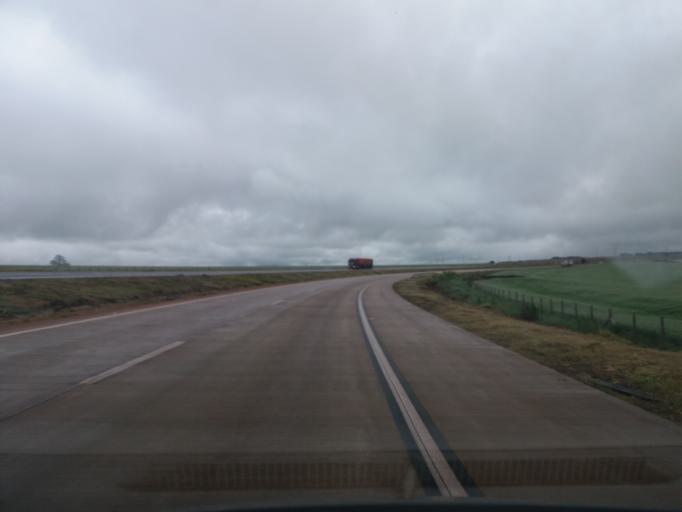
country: BR
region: Parana
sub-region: Cascavel
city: Cascavel
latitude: -25.0408
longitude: -53.5571
